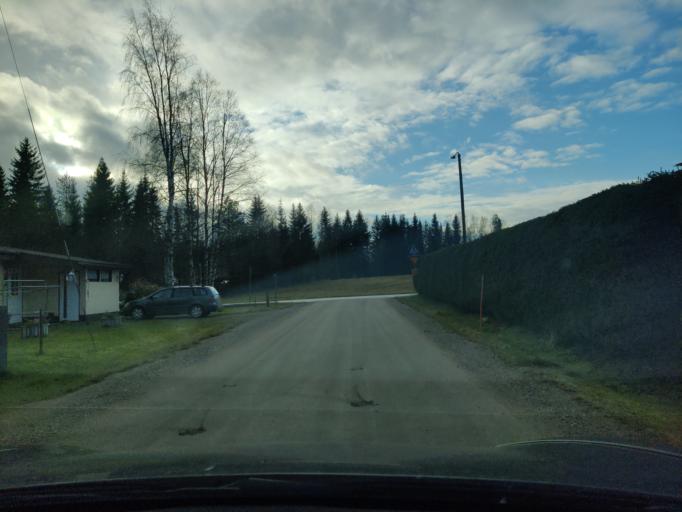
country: FI
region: Northern Savo
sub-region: Ylae-Savo
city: Kiuruvesi
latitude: 63.6438
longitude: 26.6399
